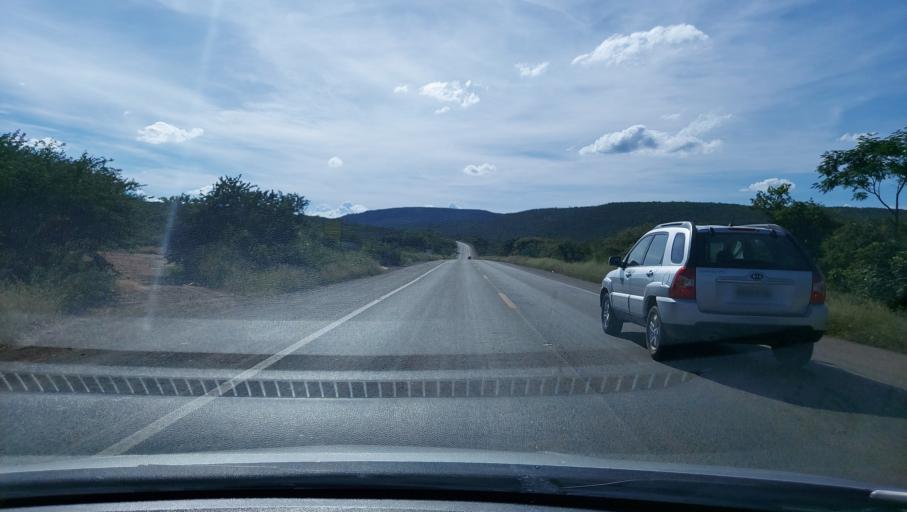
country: BR
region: Bahia
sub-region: Seabra
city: Seabra
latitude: -12.4574
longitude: -41.6503
